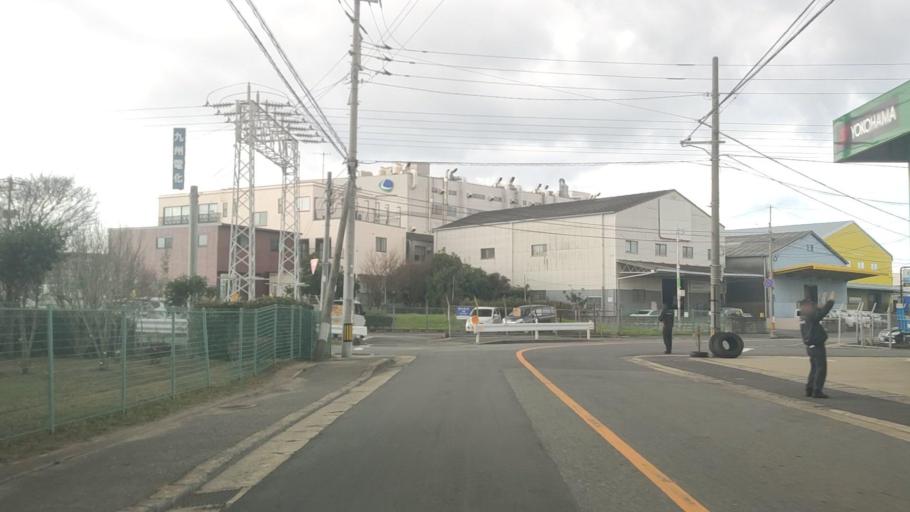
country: JP
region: Fukuoka
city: Fukuoka-shi
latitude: 33.6081
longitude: 130.4367
